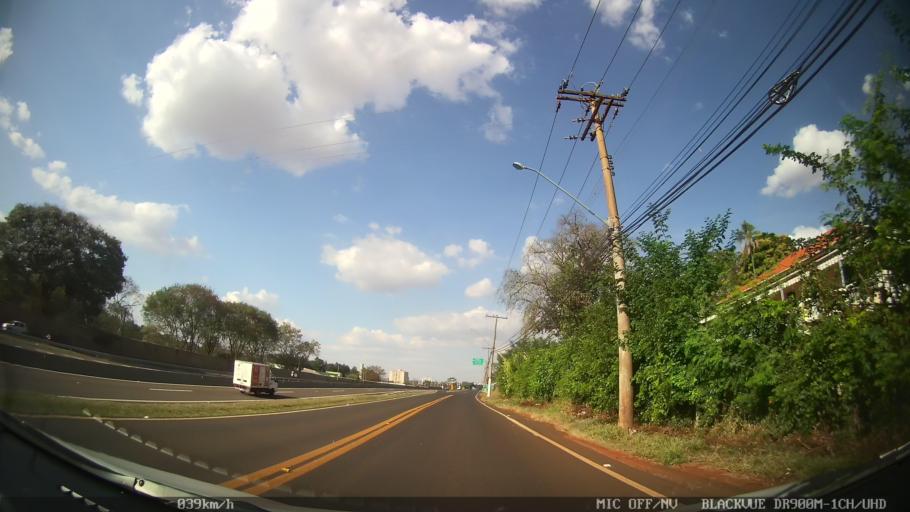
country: BR
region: Sao Paulo
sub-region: Ribeirao Preto
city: Ribeirao Preto
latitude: -21.1764
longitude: -47.8523
